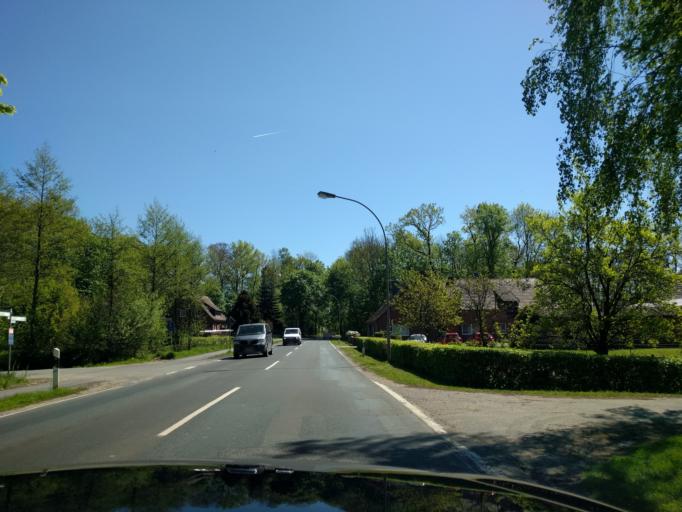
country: DE
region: Lower Saxony
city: Seevetal
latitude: 53.3978
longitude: 10.0098
